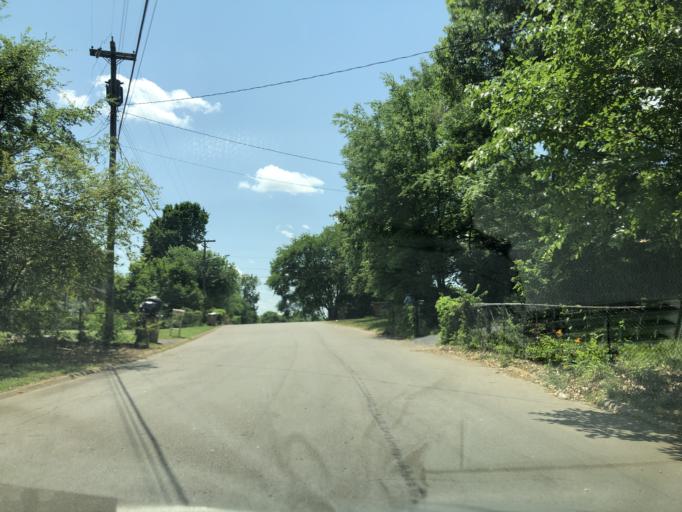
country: US
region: Tennessee
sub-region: Davidson County
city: Goodlettsville
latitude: 36.2724
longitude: -86.6962
